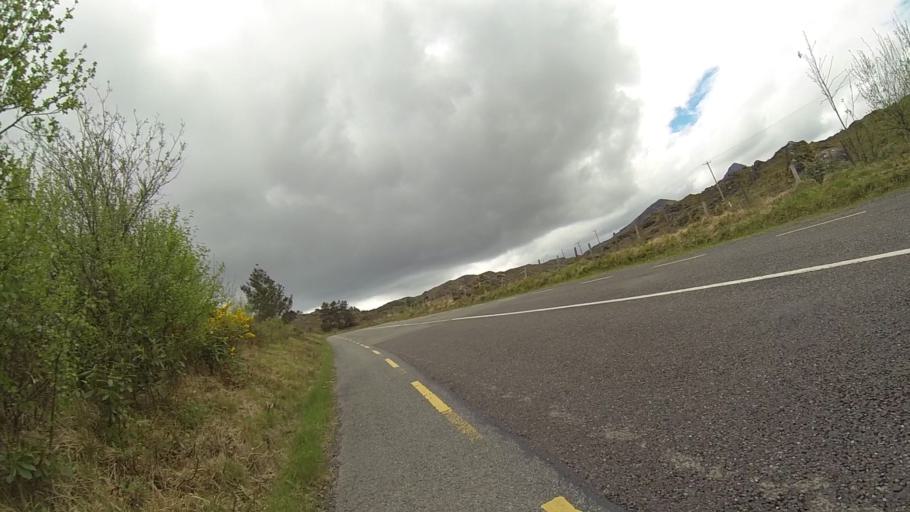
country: IE
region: Munster
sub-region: County Cork
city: Bantry
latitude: 51.7263
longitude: -9.5735
